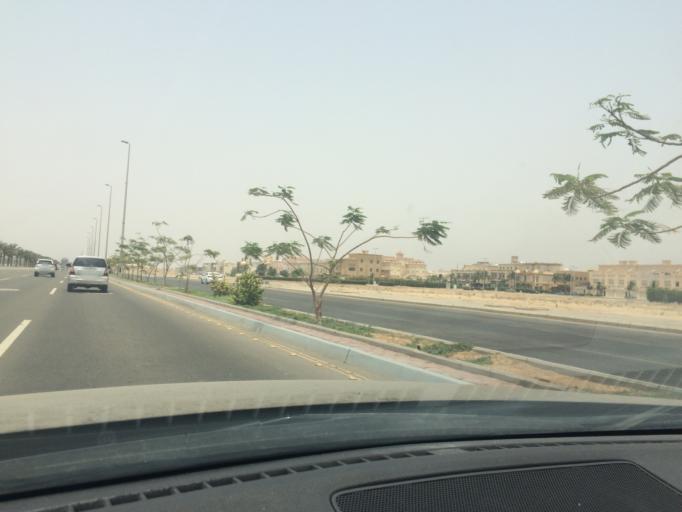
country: SA
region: Makkah
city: Jeddah
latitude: 21.6521
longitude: 39.1115
